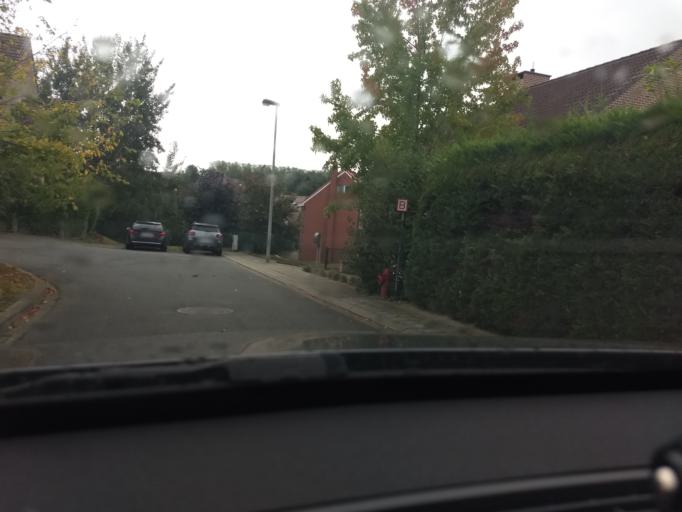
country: BE
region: Wallonia
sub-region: Province du Brabant Wallon
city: Braine-l'Alleud
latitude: 50.6762
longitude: 4.3707
